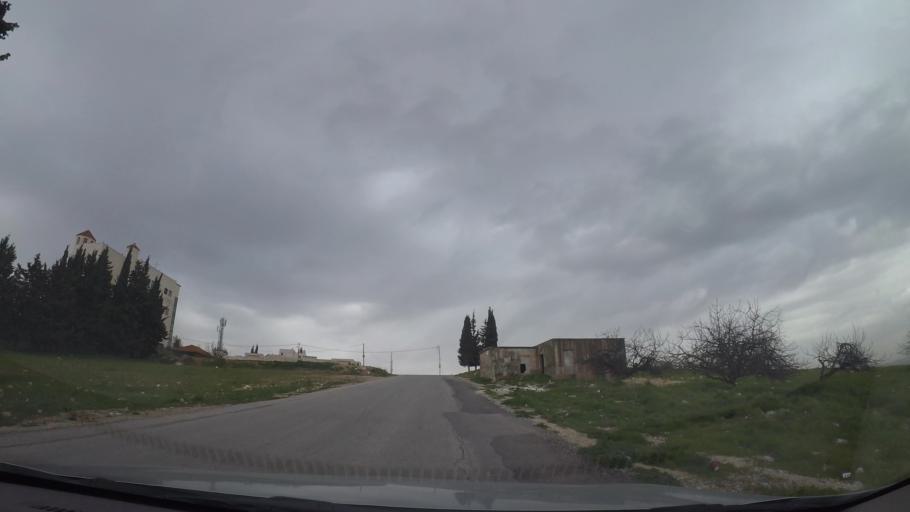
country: JO
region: Amman
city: Umm as Summaq
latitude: 31.9123
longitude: 35.8463
